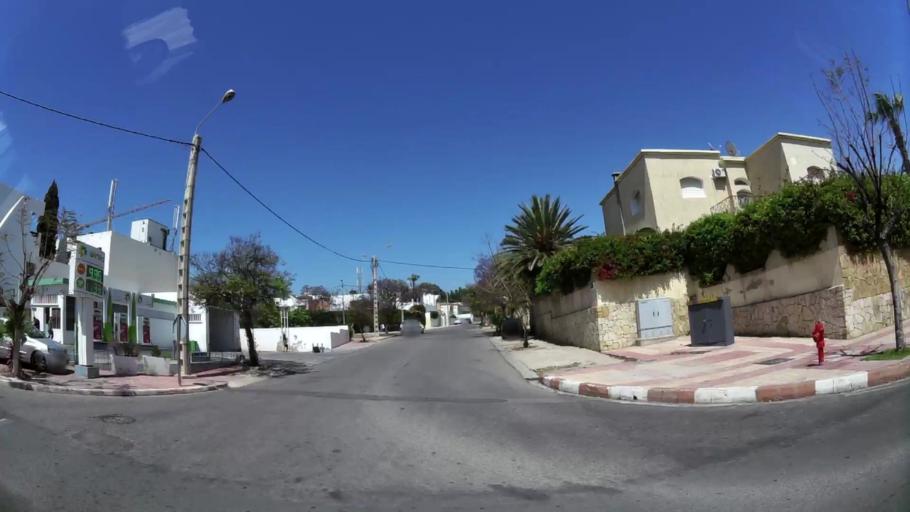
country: MA
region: Souss-Massa-Draa
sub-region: Agadir-Ida-ou-Tnan
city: Agadir
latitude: 30.4253
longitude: -9.5993
